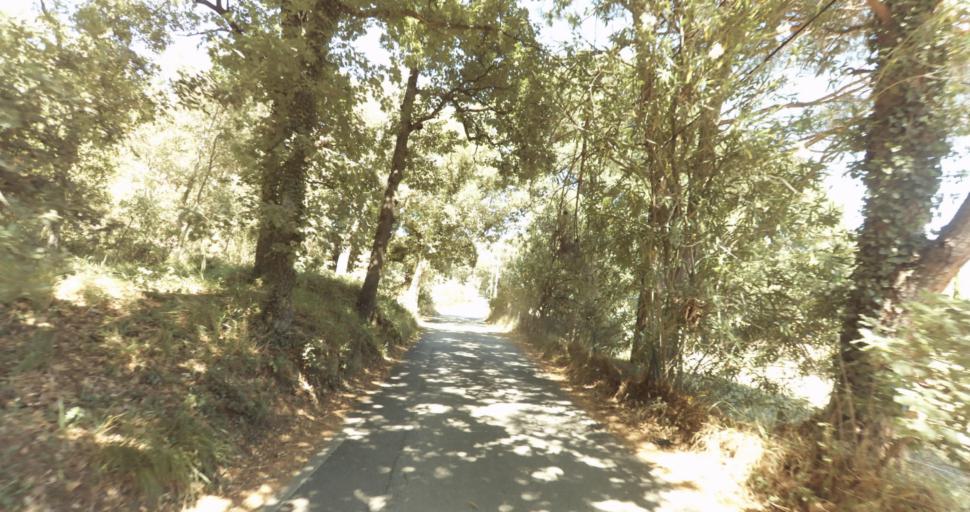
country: FR
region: Provence-Alpes-Cote d'Azur
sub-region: Departement du Var
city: Gassin
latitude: 43.2302
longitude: 6.5718
